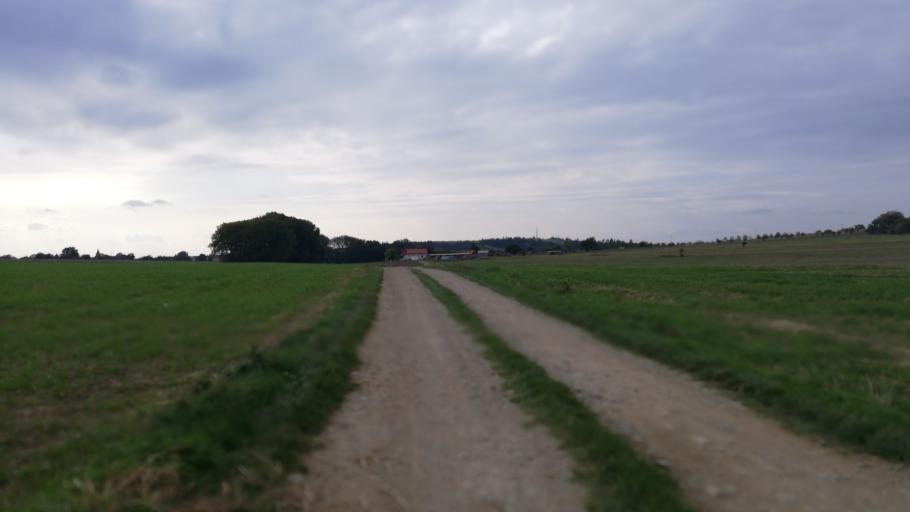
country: SK
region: Trnavsky
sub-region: Okres Skalica
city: Skalica
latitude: 48.8184
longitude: 17.2562
